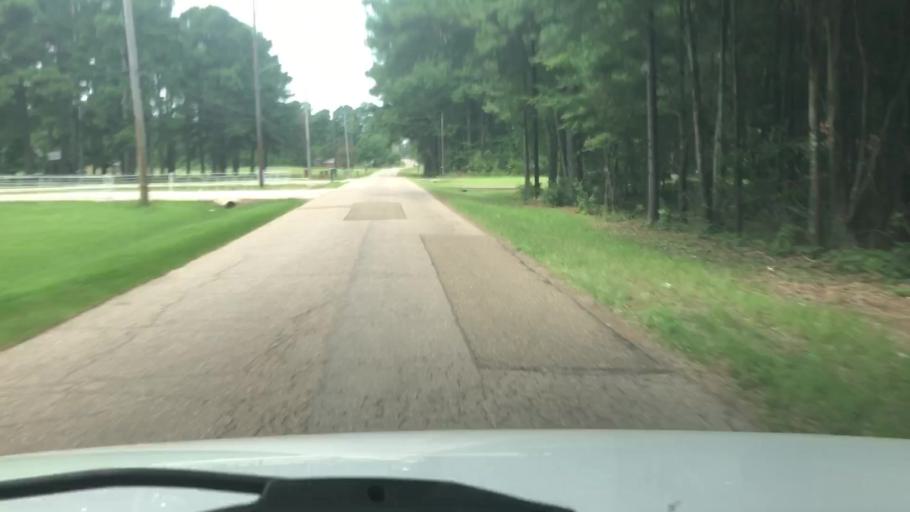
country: US
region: Texas
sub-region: Bowie County
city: Wake Village
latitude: 33.3889
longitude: -94.0821
